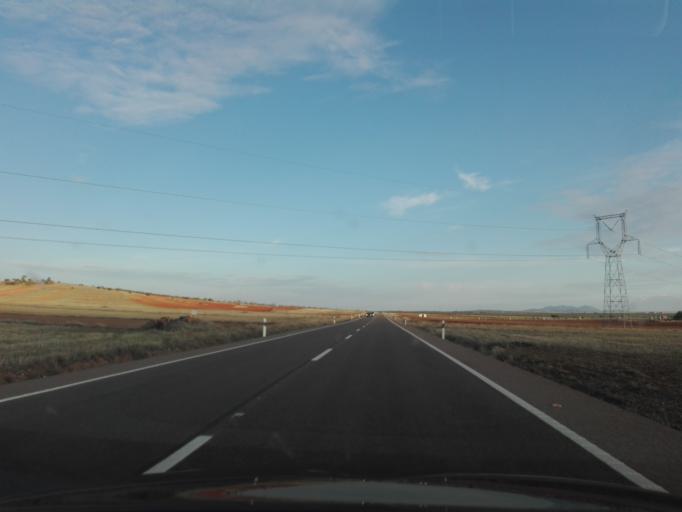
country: ES
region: Extremadura
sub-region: Provincia de Badajoz
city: Usagre
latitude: 38.3580
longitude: -6.2127
